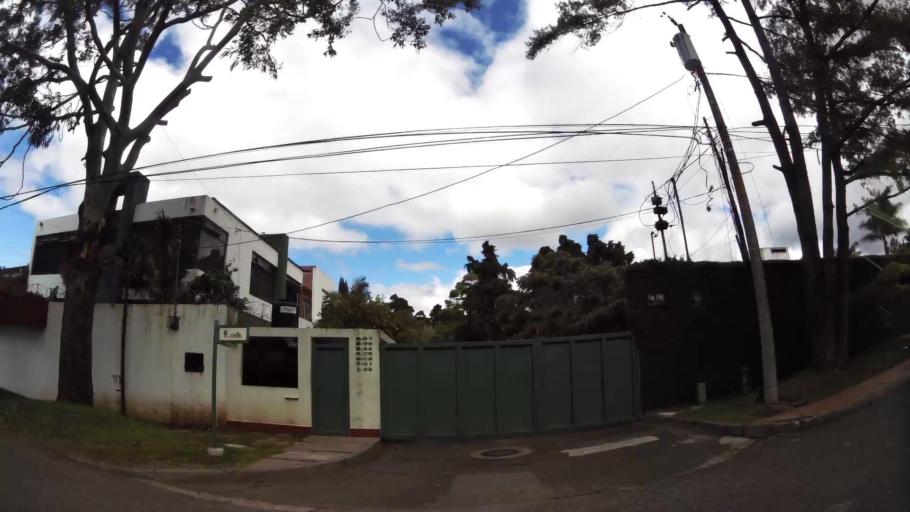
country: GT
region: Guatemala
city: Santa Catarina Pinula
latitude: 14.5828
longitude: -90.5122
